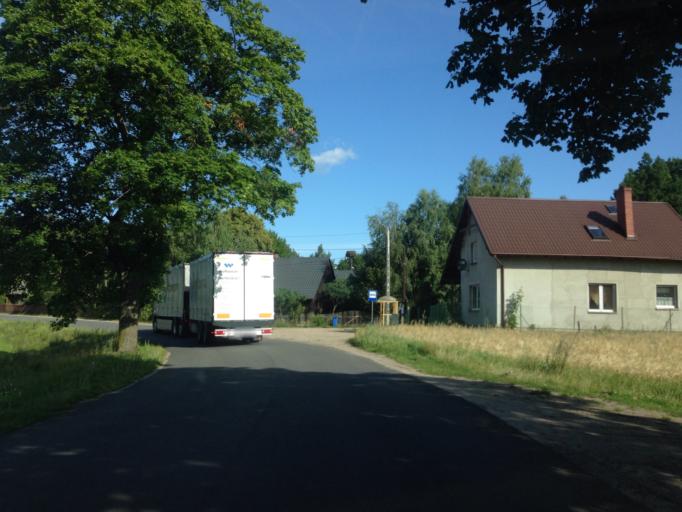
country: PL
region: Pomeranian Voivodeship
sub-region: Powiat starogardzki
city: Osiek
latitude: 53.7405
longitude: 18.4343
